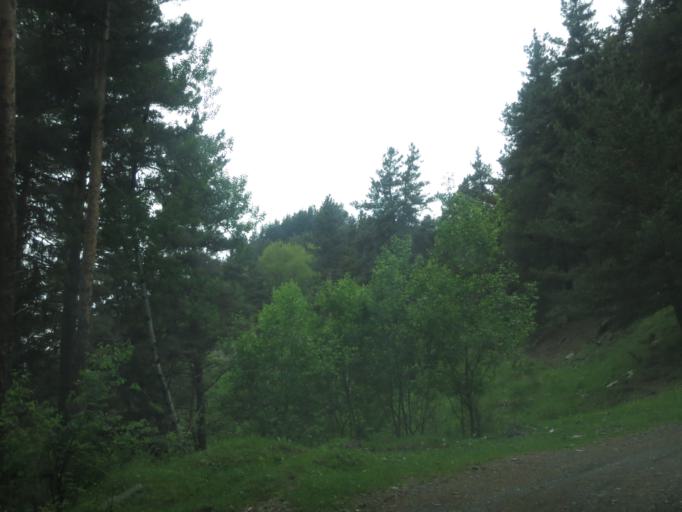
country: RU
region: Chechnya
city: Itum-Kali
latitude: 42.3664
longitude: 45.6521
